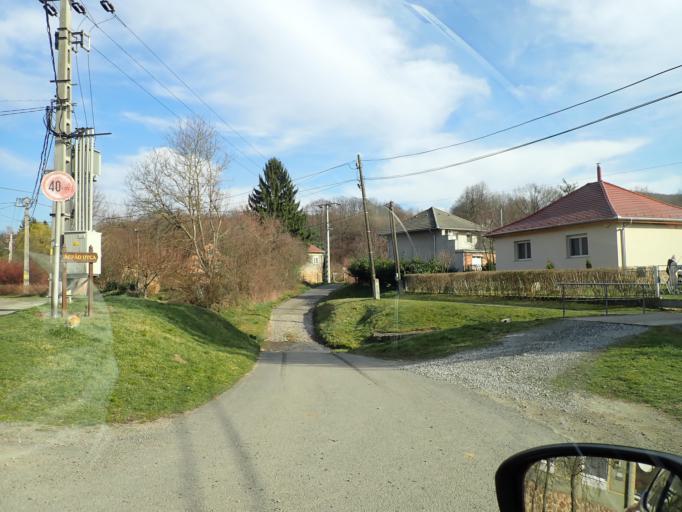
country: HU
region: Baranya
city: Komlo
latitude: 46.1614
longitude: 18.2453
